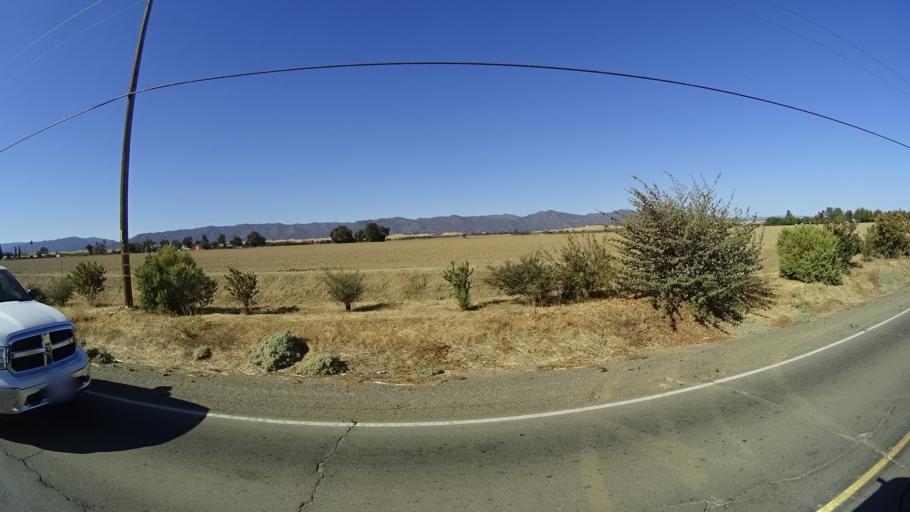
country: US
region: California
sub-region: Yolo County
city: Winters
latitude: 38.5882
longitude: -121.9714
